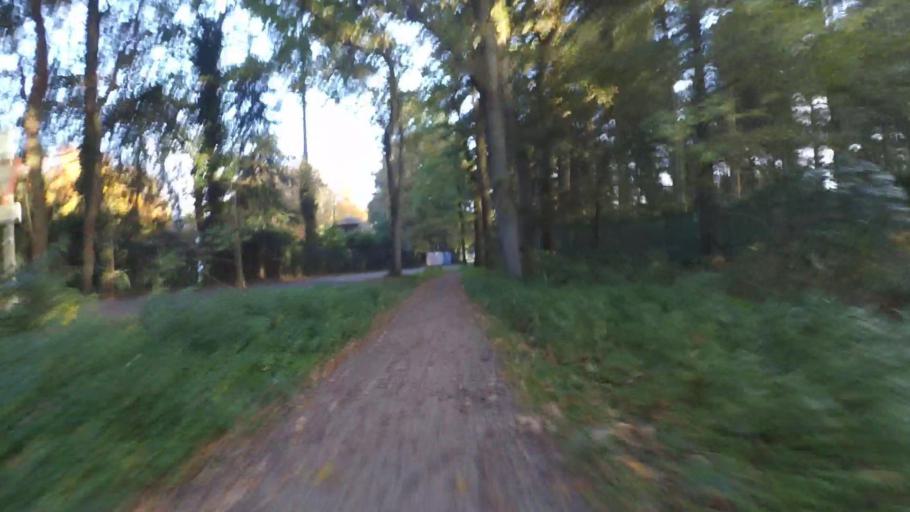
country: NL
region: Utrecht
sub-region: Gemeente Baarn
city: Baarn
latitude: 52.2007
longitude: 5.2527
